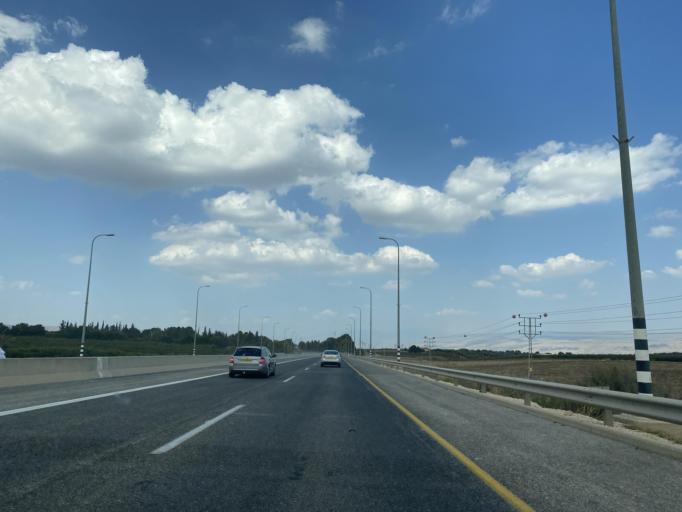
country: IL
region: Northern District
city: Rosh Pinna
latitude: 32.9973
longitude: 35.5644
